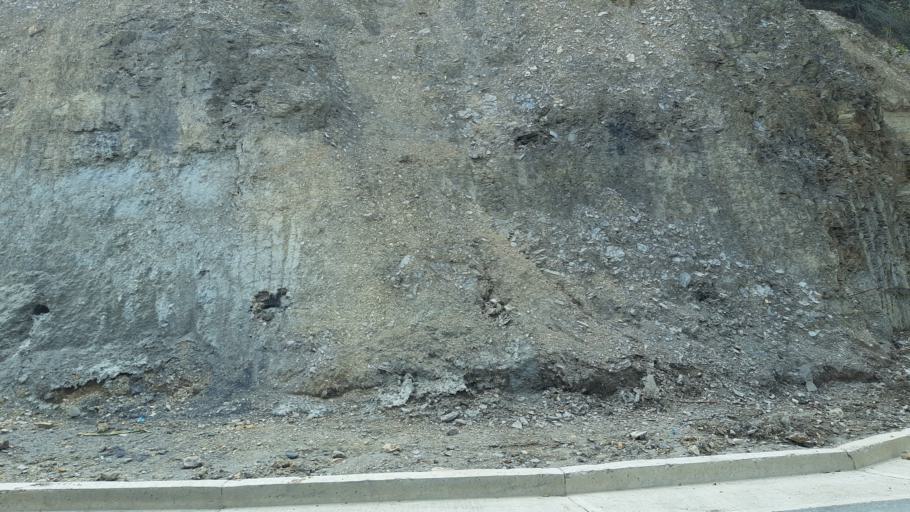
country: CO
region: Boyaca
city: Santa Sofia
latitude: 5.7833
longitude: -73.6029
